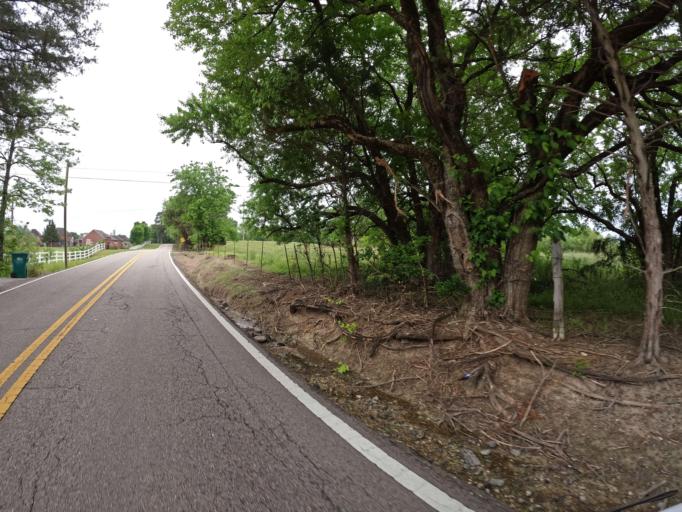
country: US
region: Mississippi
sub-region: Lee County
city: Tupelo
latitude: 34.2892
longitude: -88.7640
